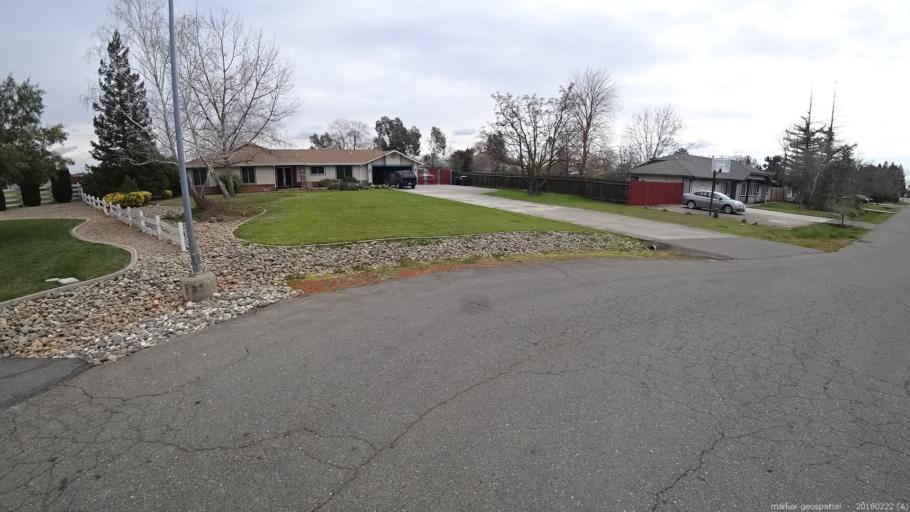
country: US
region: California
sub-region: Sacramento County
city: Rio Linda
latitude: 38.7211
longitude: -121.4121
